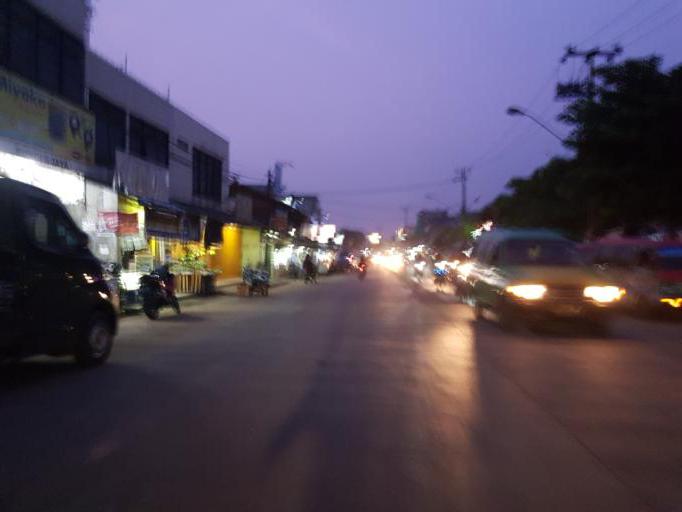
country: ID
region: West Java
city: Serpong
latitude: -6.3218
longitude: 106.6634
